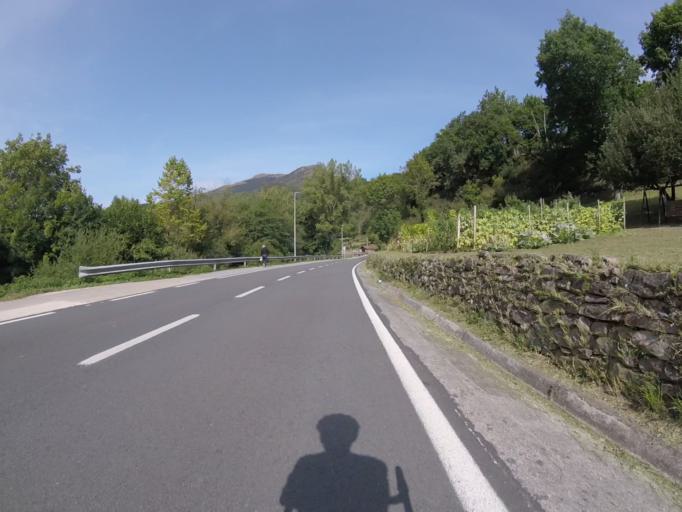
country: ES
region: Navarre
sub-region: Provincia de Navarra
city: Elgorriaga
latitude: 43.1372
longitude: -1.6817
